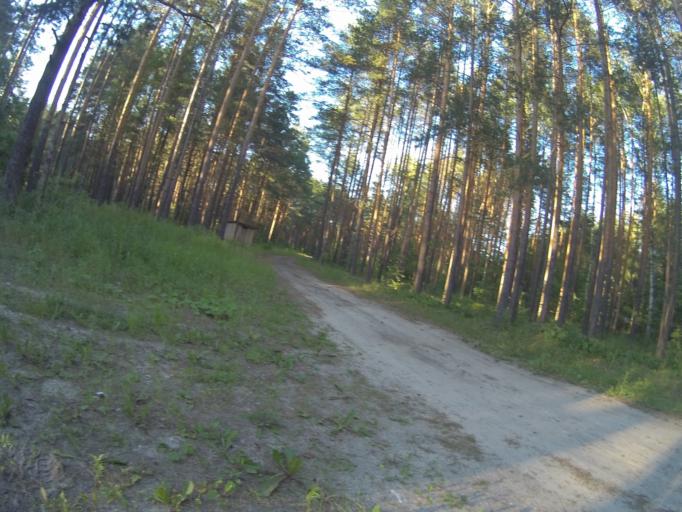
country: RU
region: Vladimir
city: Kommunar
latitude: 56.1420
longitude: 40.4933
